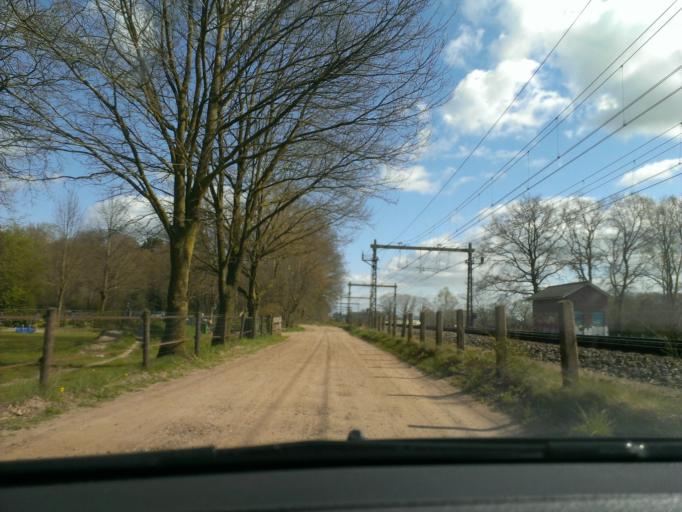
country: NL
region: Overijssel
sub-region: Gemeente Almelo
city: Almelo
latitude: 52.3263
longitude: 6.6964
